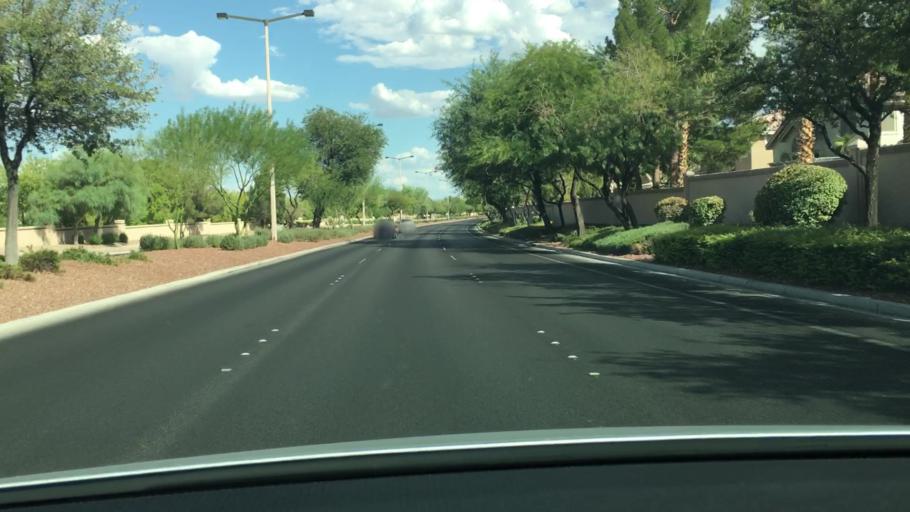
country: US
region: Nevada
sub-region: Clark County
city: Summerlin South
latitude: 36.2051
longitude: -115.2932
